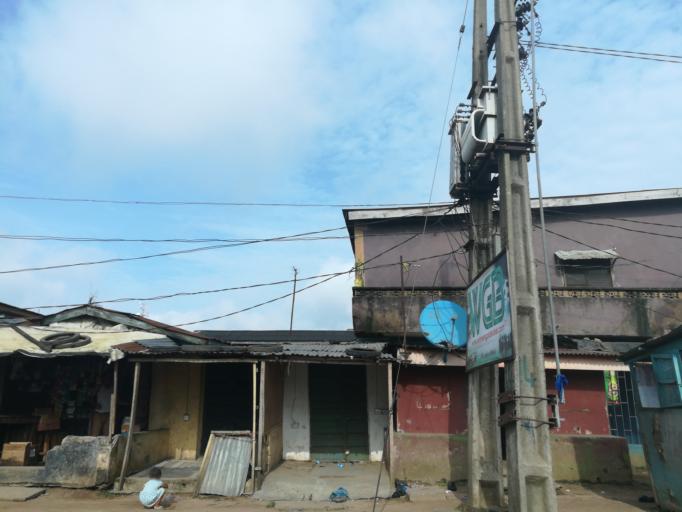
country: NG
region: Lagos
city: Agege
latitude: 6.6194
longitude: 3.3127
